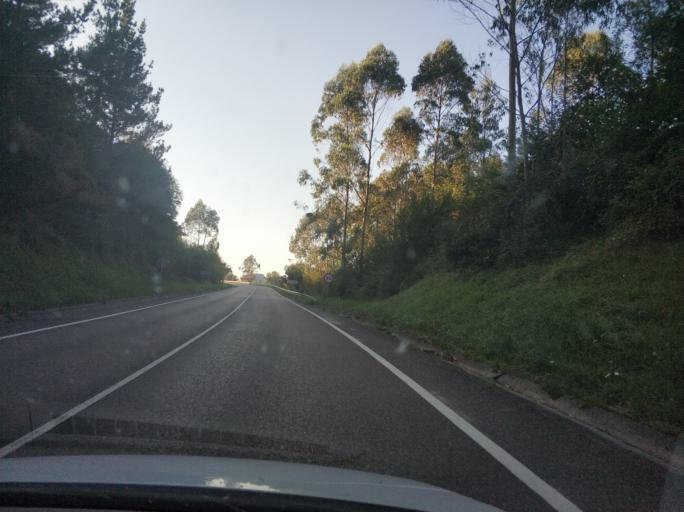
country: ES
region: Cantabria
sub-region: Provincia de Cantabria
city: Cabezon de la Sal
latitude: 43.3377
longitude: -4.2710
